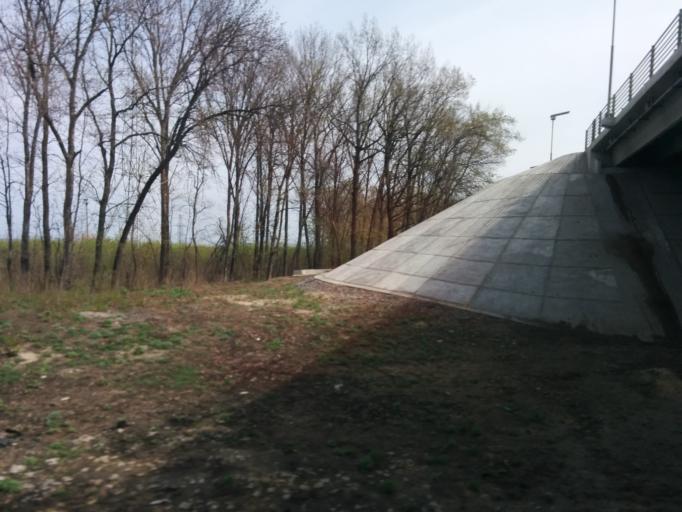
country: RU
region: Tambov
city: Komsomolets
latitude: 52.7660
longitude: 41.3226
